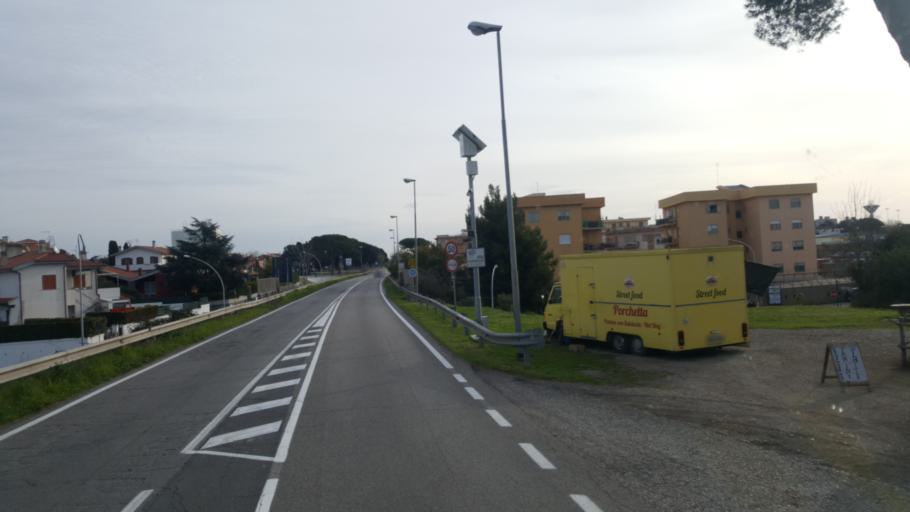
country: IT
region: Latium
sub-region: Provincia di Viterbo
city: Montalto di Castro
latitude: 42.3482
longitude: 11.6069
